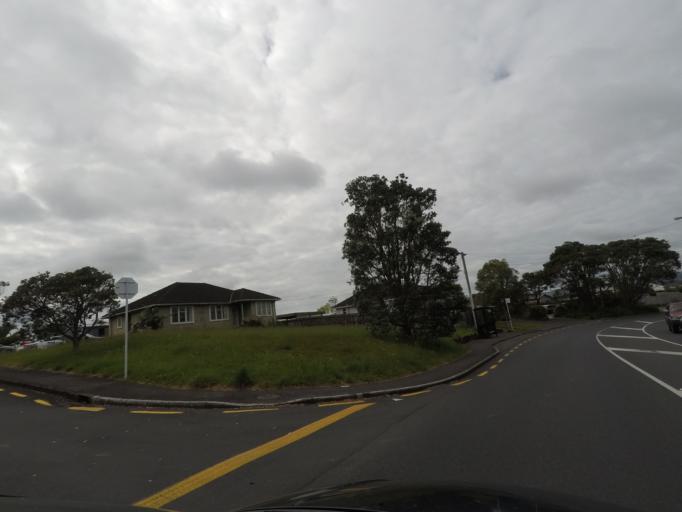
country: NZ
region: Auckland
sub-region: Auckland
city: Rosebank
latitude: -36.8457
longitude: 174.6081
